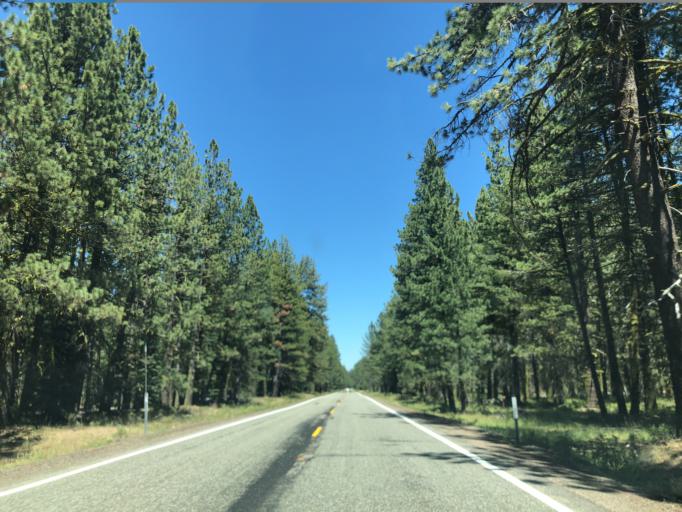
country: US
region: California
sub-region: Shasta County
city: Burney
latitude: 40.6051
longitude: -121.5255
